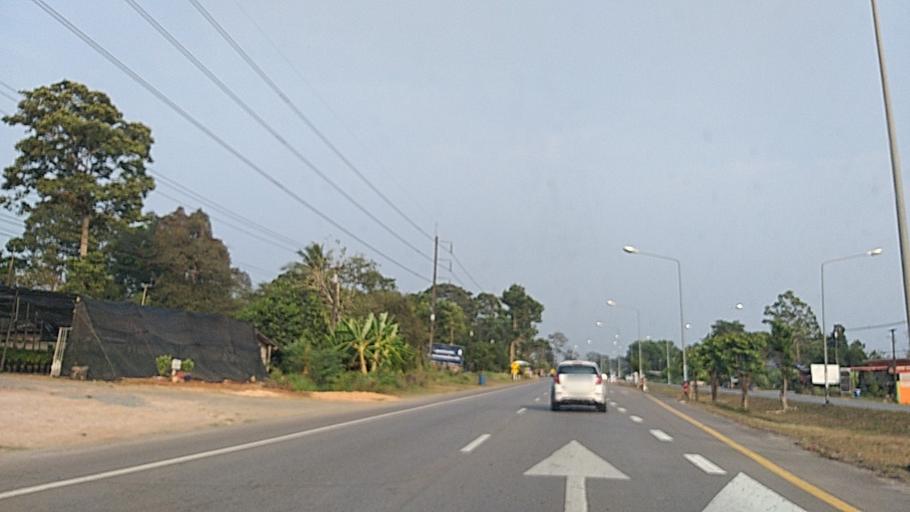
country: TH
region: Chanthaburi
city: Khlung
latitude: 12.4551
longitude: 102.2765
